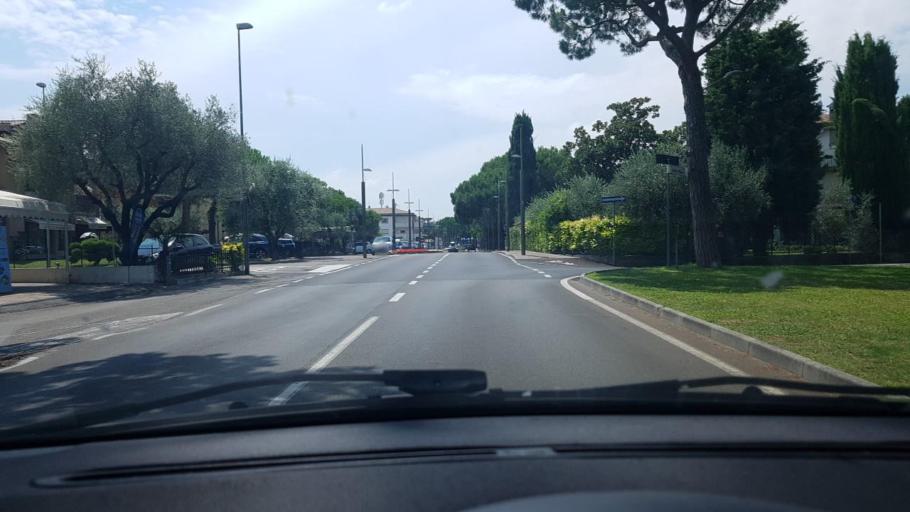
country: IT
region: Lombardy
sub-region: Provincia di Brescia
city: Sirmione
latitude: 45.4707
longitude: 10.6084
